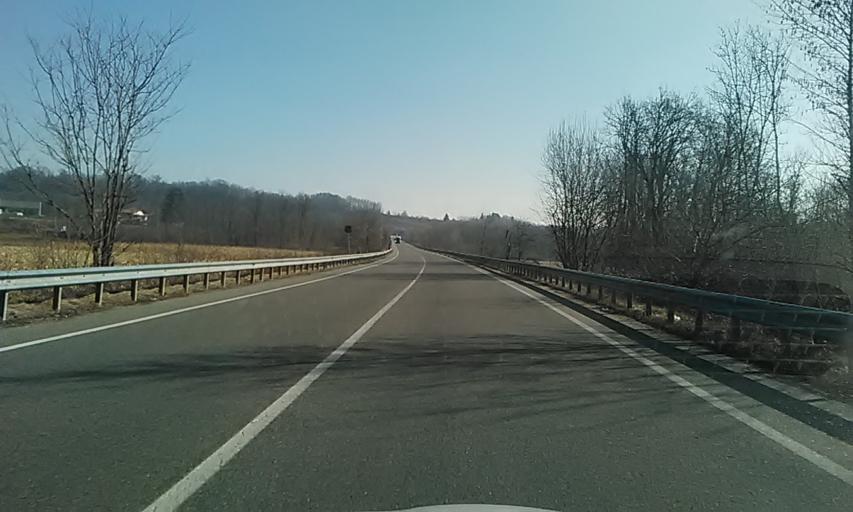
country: IT
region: Piedmont
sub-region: Provincia di Novara
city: Prato Sesia
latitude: 45.6600
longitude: 8.3718
